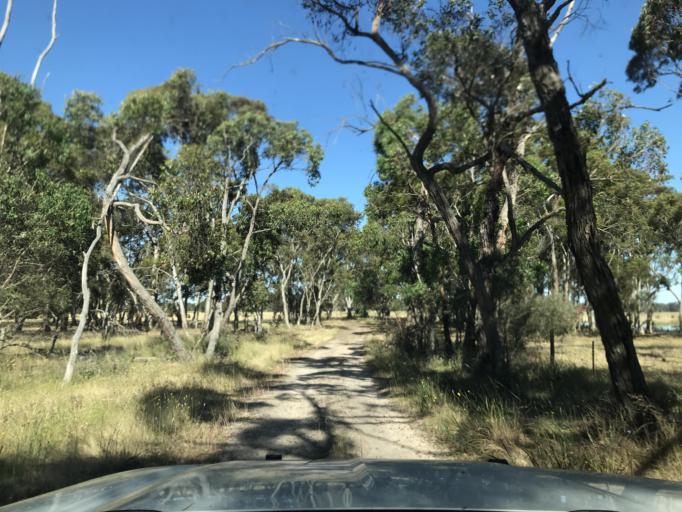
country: AU
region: South Australia
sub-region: Wattle Range
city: Penola
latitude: -37.0805
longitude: 141.3847
